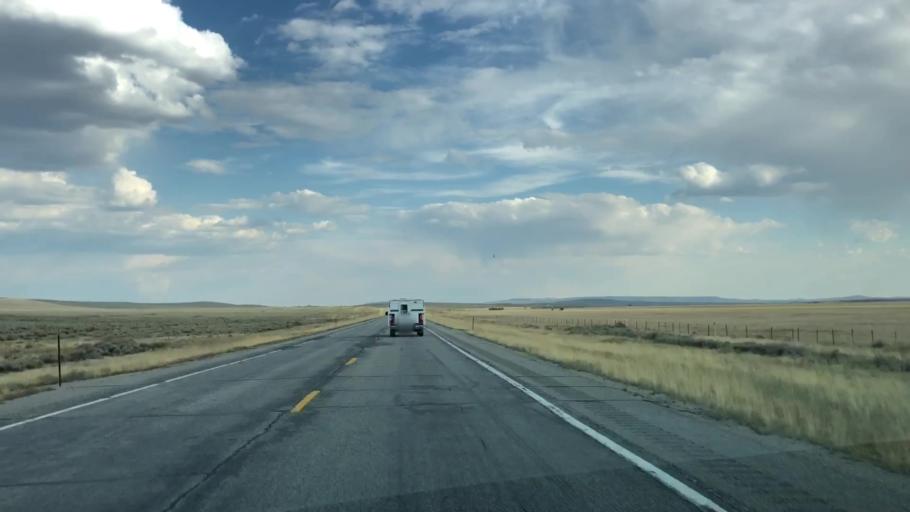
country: US
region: Wyoming
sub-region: Sublette County
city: Pinedale
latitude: 43.0435
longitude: -110.1434
